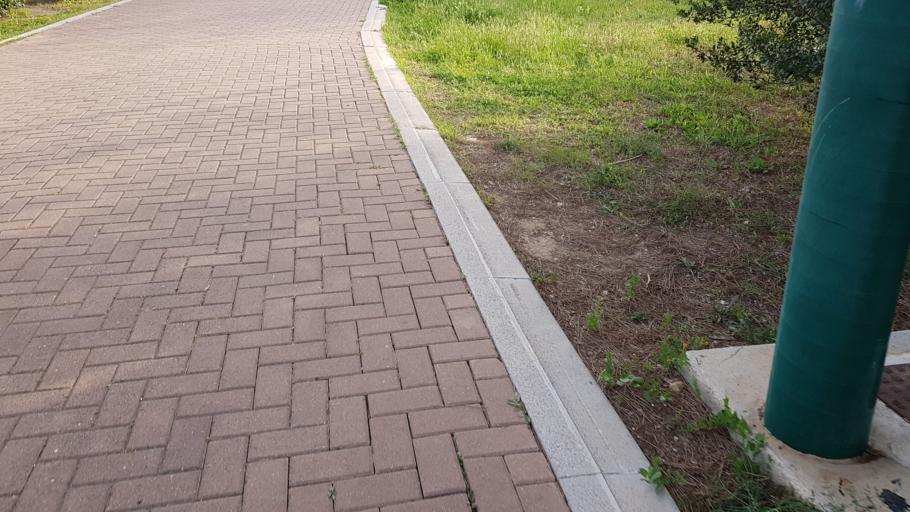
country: IT
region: Apulia
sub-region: Provincia di Brindisi
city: Brindisi
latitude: 40.6393
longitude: 17.9228
